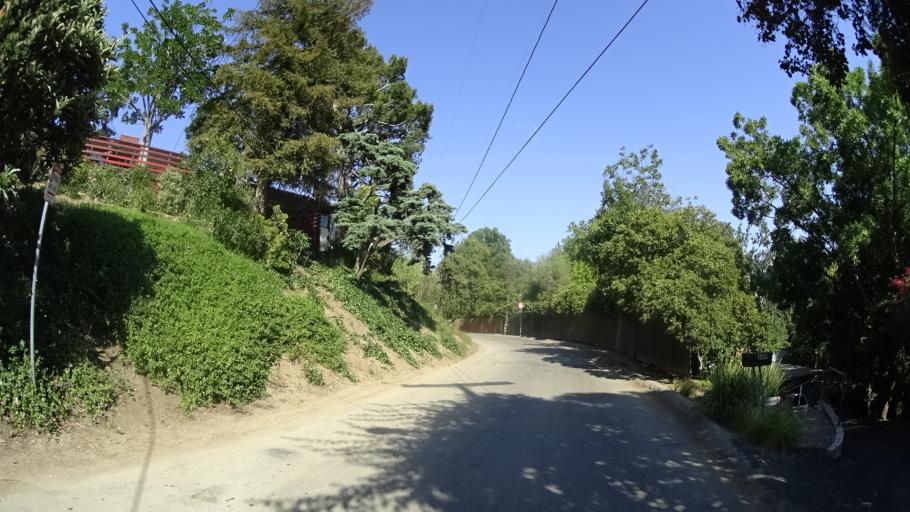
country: US
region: California
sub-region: Los Angeles County
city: Universal City
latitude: 34.1355
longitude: -118.3778
